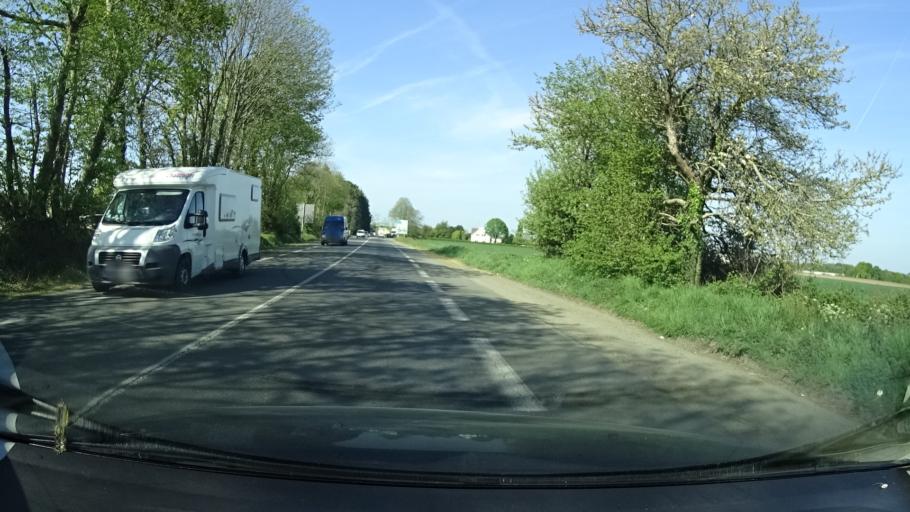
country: FR
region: Brittany
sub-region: Departement du Finistere
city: Quimperle
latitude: 47.8684
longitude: -3.5774
